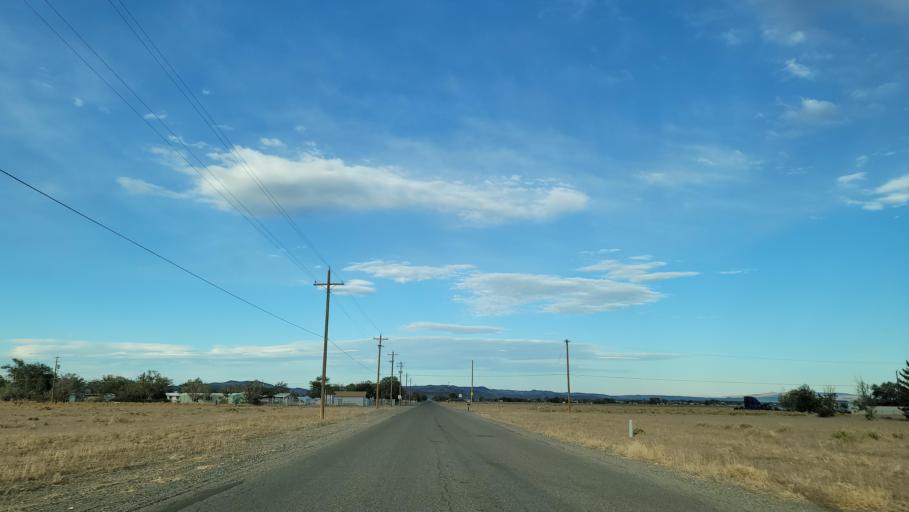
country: US
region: Nevada
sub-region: Lyon County
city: Silver Springs
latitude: 39.3899
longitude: -119.2522
